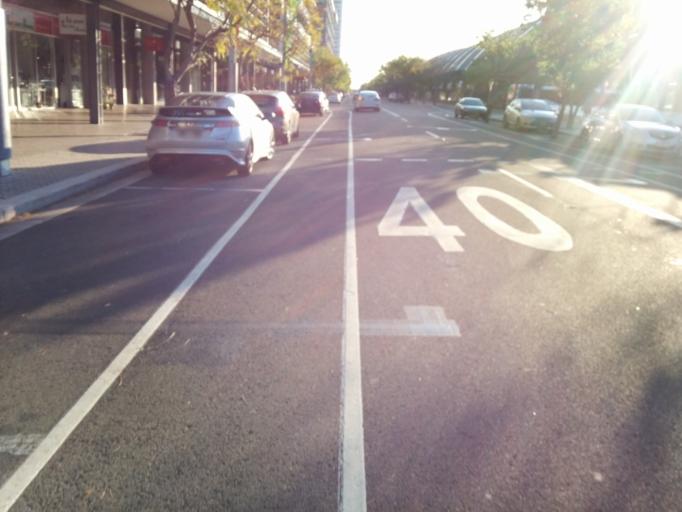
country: AU
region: New South Wales
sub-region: Canada Bay
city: Concord West
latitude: -33.8461
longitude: 151.0716
